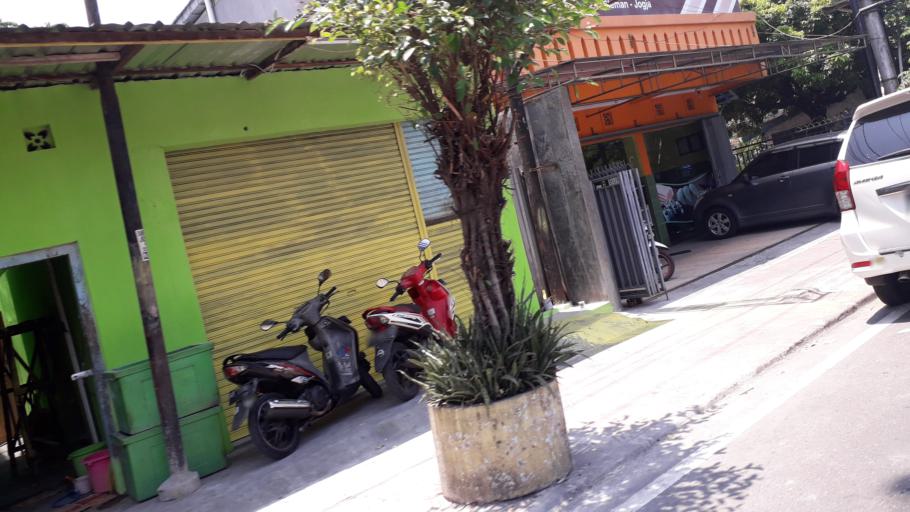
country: ID
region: Daerah Istimewa Yogyakarta
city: Yogyakarta
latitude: -7.7688
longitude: 110.3688
